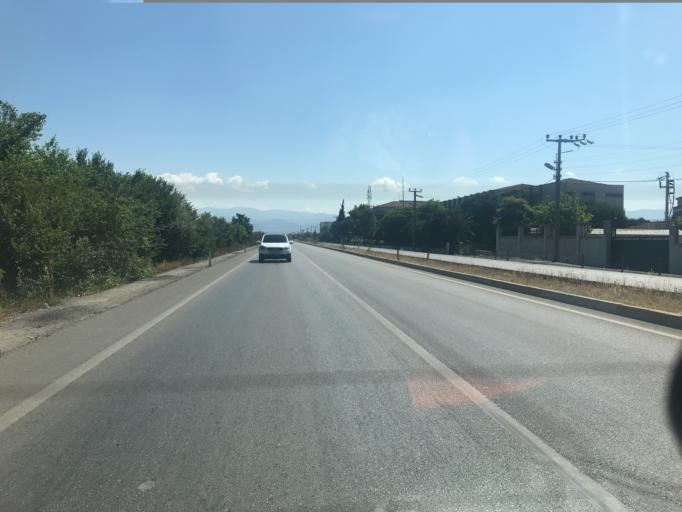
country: TR
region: Manisa
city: Akhisar
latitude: 38.9043
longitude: 27.8052
